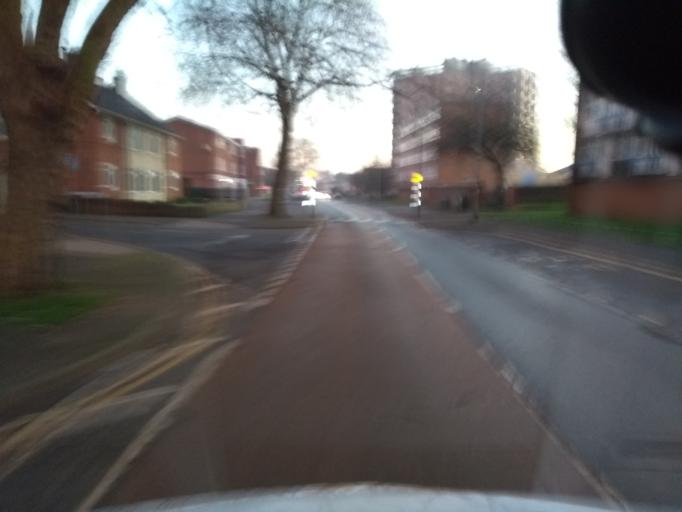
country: GB
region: England
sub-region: Somerset
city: Bridgwater
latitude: 51.1254
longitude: -3.0118
